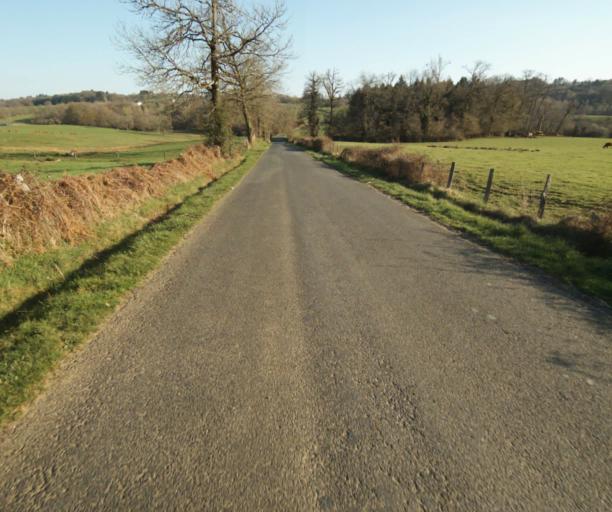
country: FR
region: Limousin
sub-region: Departement de la Correze
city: Saint-Clement
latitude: 45.3347
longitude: 1.6549
